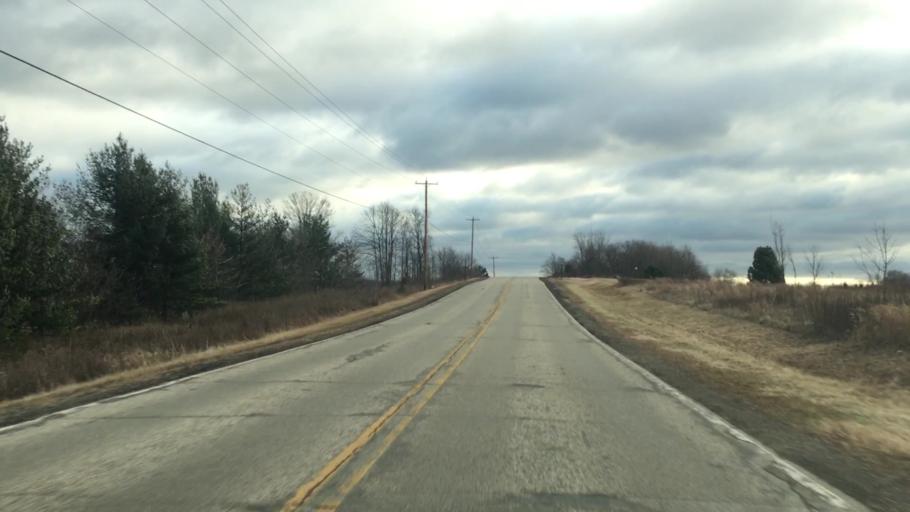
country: US
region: Wisconsin
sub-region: Washington County
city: Richfield
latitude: 43.2366
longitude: -88.2309
